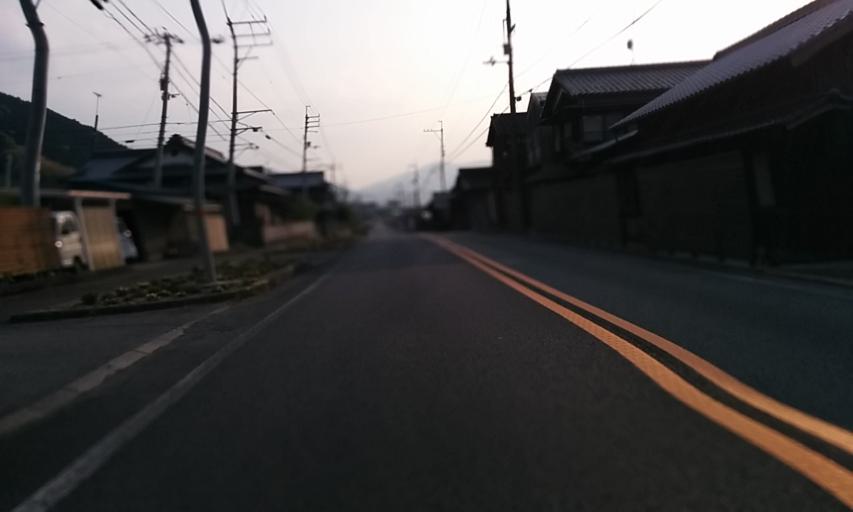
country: JP
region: Ehime
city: Saijo
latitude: 33.8800
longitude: 133.0723
